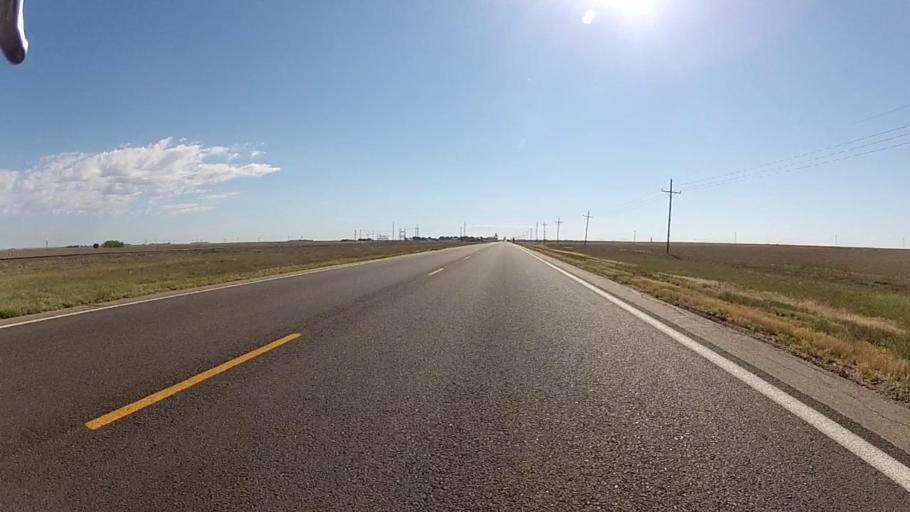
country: US
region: Kansas
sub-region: Gray County
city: Cimarron
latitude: 37.5853
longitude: -100.4923
